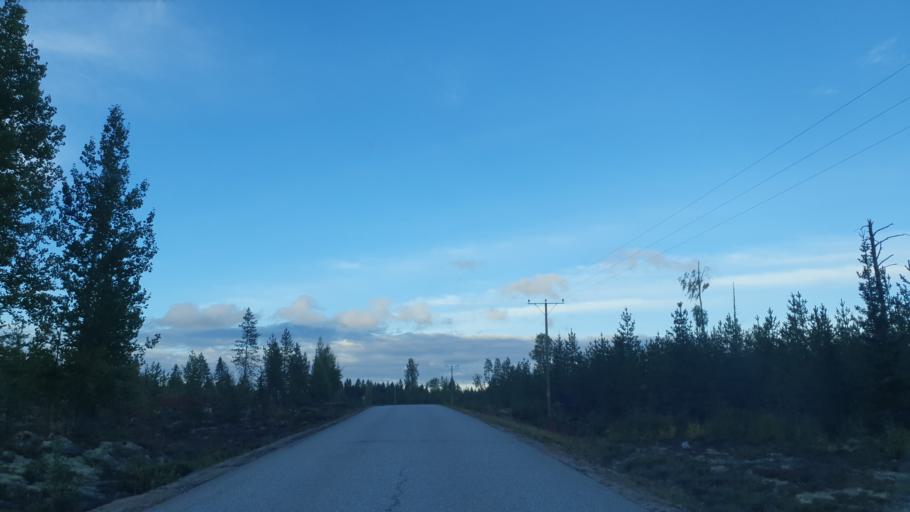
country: FI
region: Kainuu
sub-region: Kehys-Kainuu
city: Kuhmo
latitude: 64.4174
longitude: 29.9600
